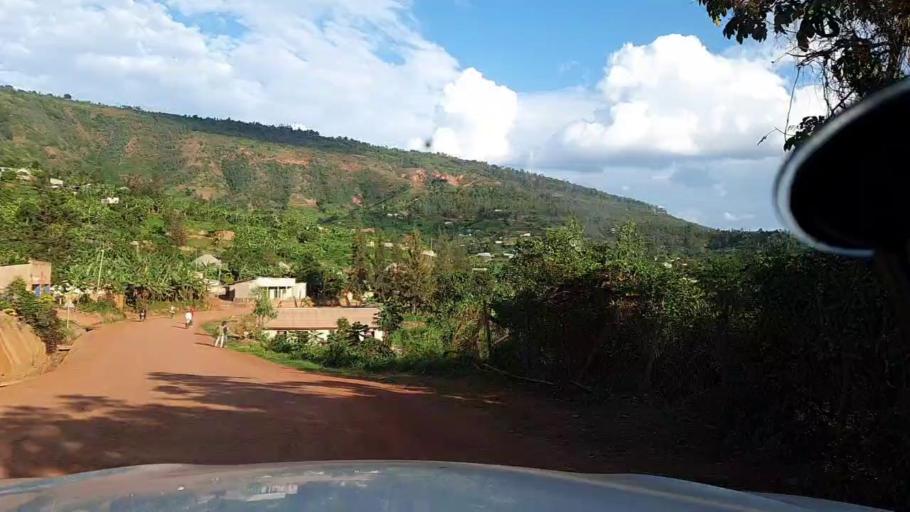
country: RW
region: Kigali
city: Kigali
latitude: -1.9152
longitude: 29.9869
